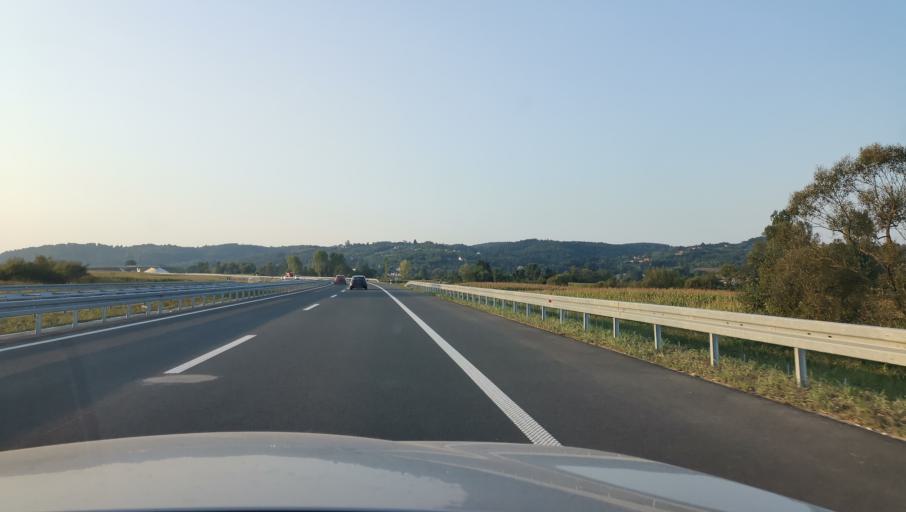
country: RS
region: Central Serbia
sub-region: Kolubarski Okrug
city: Lajkovac
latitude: 44.3242
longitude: 20.2129
